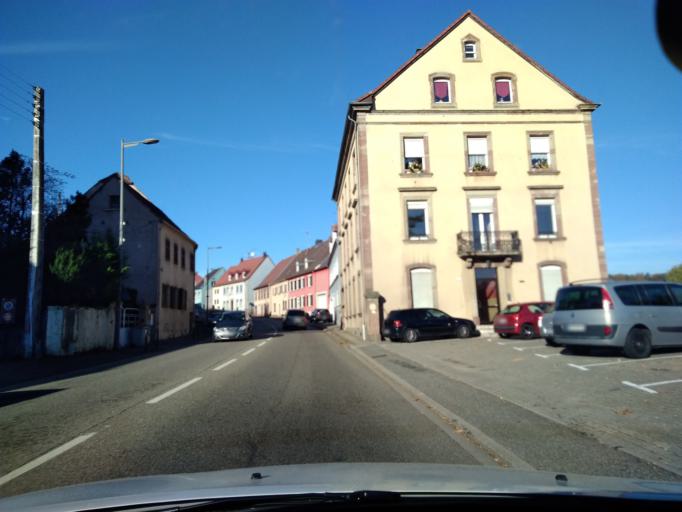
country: FR
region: Lorraine
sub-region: Departement de la Moselle
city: Sarreguemines
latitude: 49.1130
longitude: 7.0498
